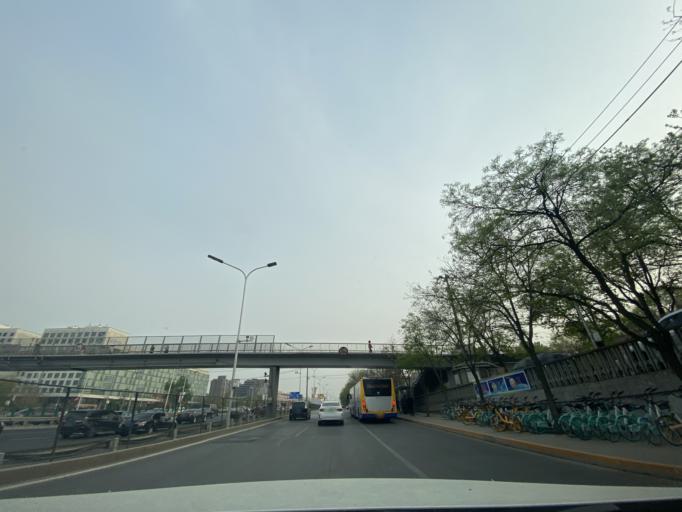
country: CN
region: Beijing
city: Sijiqing
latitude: 39.9321
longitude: 116.2684
